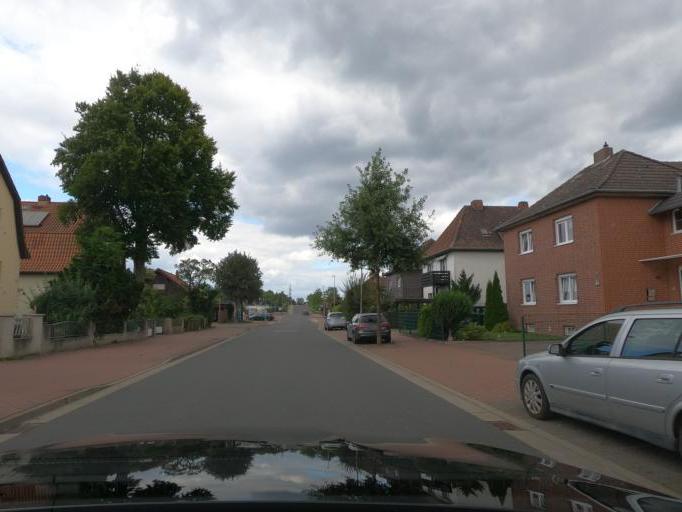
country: DE
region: Lower Saxony
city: Lehrte
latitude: 52.3740
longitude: 9.9065
